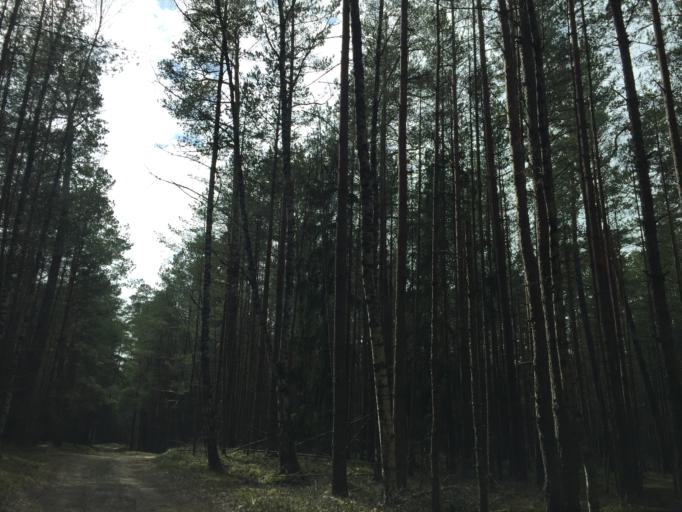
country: LV
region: Salacgrivas
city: Salacgriva
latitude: 57.6905
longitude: 24.3608
